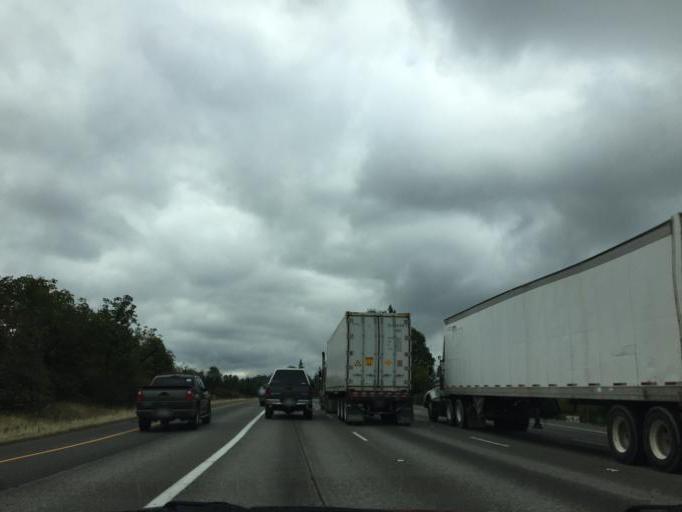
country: US
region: Washington
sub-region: King County
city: Lakeland North
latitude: 47.3604
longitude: -122.2961
